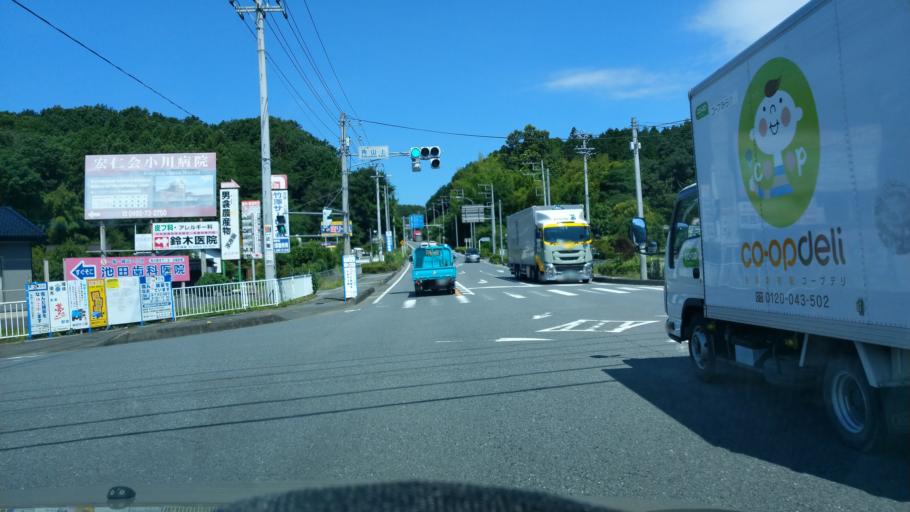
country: JP
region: Saitama
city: Ogawa
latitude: 36.0705
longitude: 139.2517
